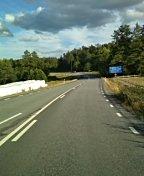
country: SE
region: Uppsala
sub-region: Habo Kommun
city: Balsta
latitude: 59.6278
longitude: 17.4888
